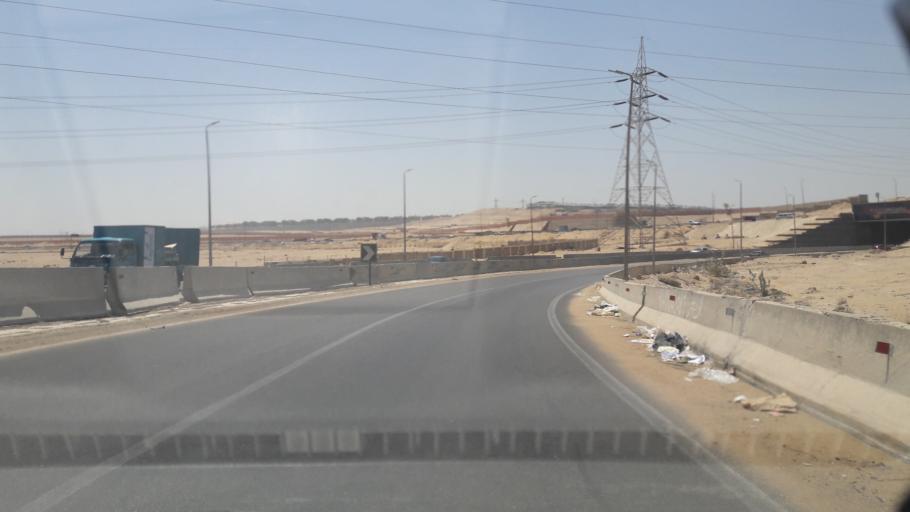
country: EG
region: Al Jizah
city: Al Jizah
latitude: 29.9976
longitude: 31.0927
